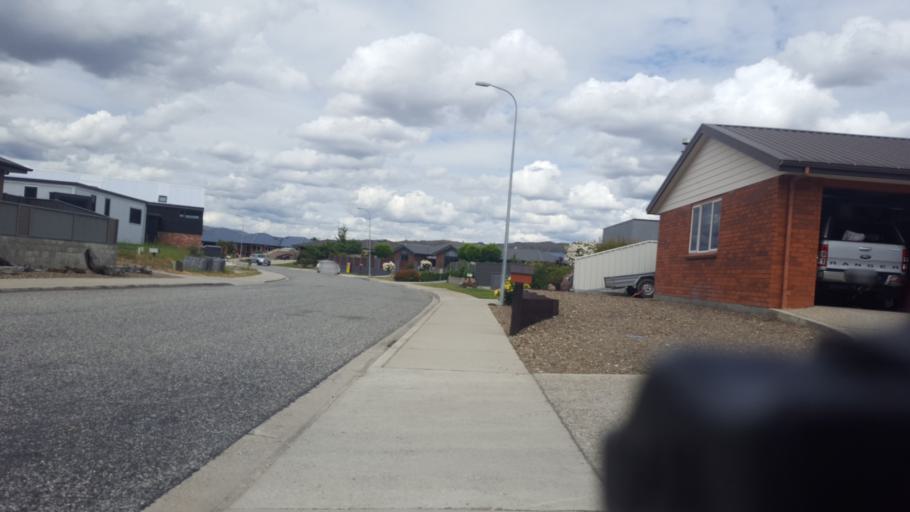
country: NZ
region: Otago
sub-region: Queenstown-Lakes District
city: Wanaka
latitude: -45.2455
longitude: 169.3740
